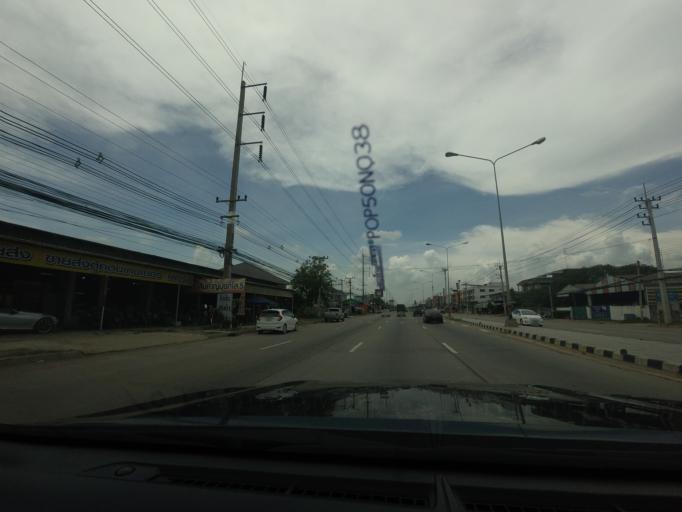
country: TH
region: Nakhon Pathom
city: Nakhon Pathom
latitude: 13.8505
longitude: 100.0194
